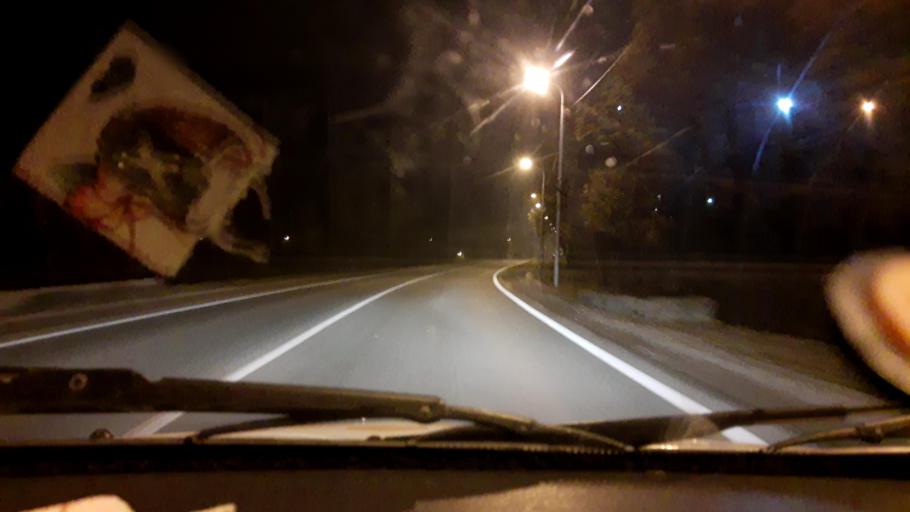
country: RU
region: Bashkortostan
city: Ufa
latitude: 54.8343
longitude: 56.1340
